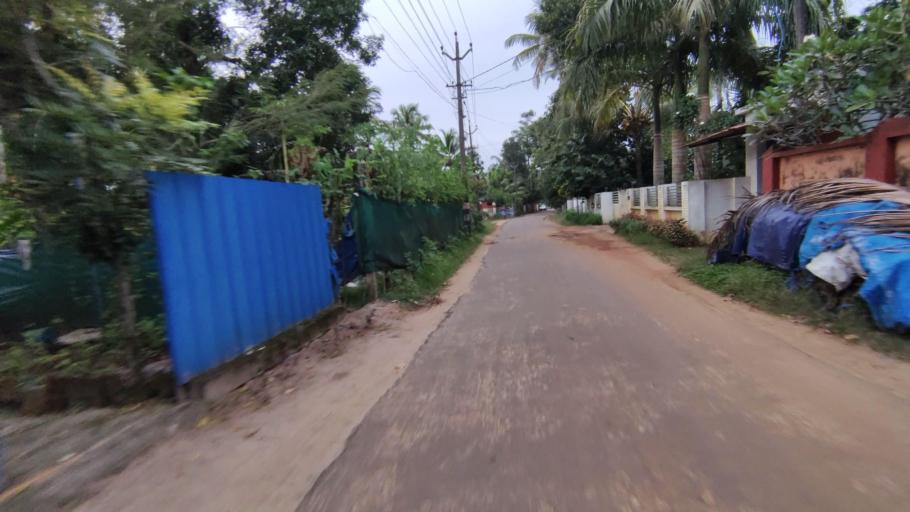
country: IN
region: Kerala
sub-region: Alappuzha
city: Shertallai
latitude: 9.6596
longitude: 76.3632
